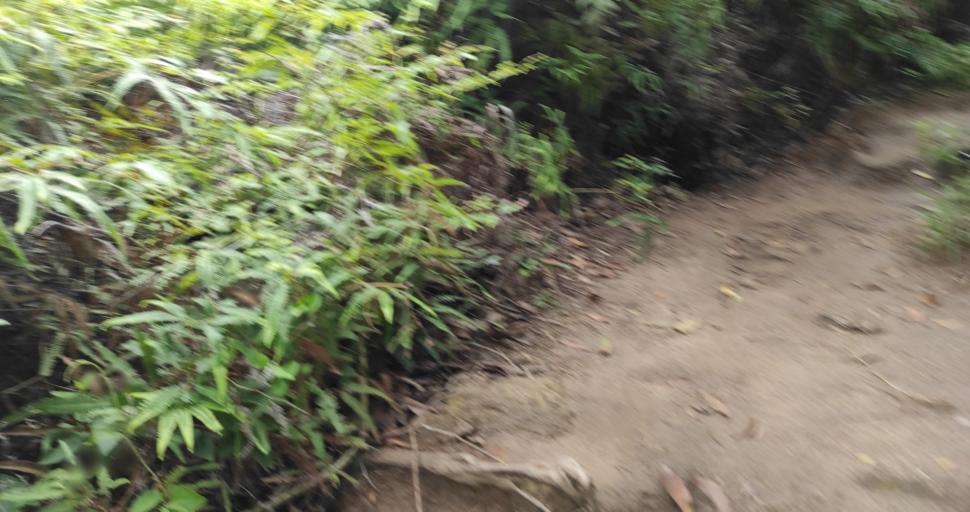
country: BR
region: Santa Catarina
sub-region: Porto Belo
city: Porto Belo
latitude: -27.2026
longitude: -48.4954
